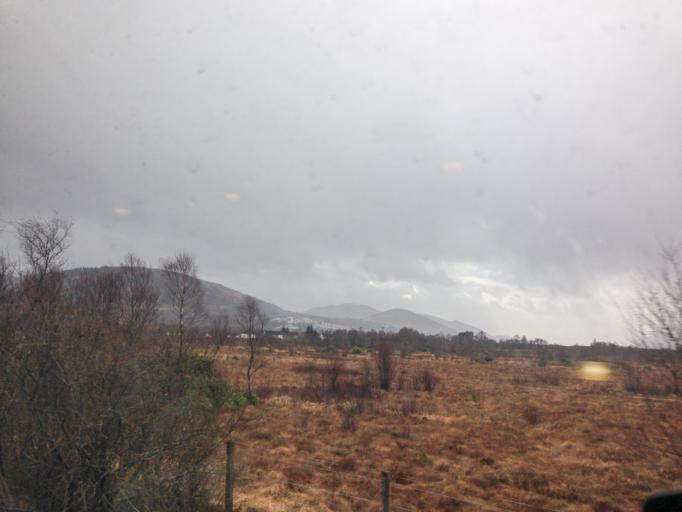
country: GB
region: Scotland
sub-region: Highland
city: Fort William
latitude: 56.8419
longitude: -5.0929
